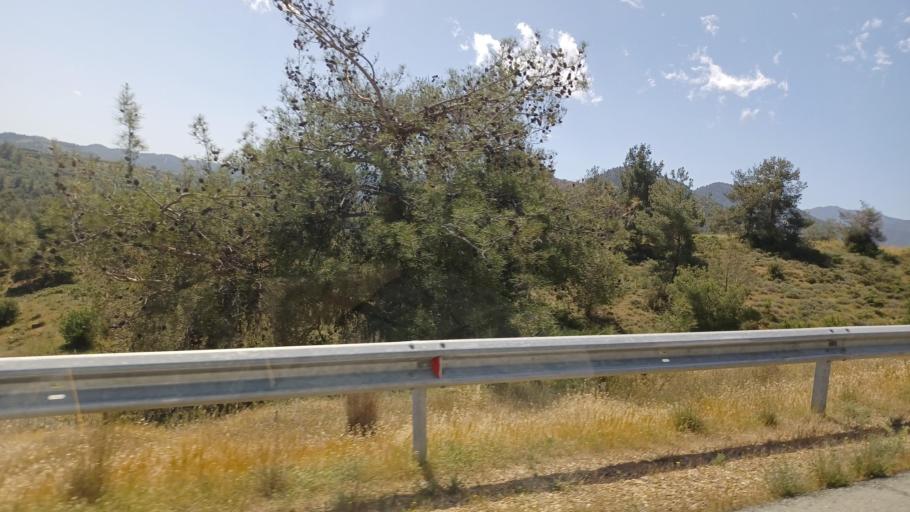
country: CY
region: Lefkosia
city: Astromeritis
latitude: 35.0508
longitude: 33.0214
